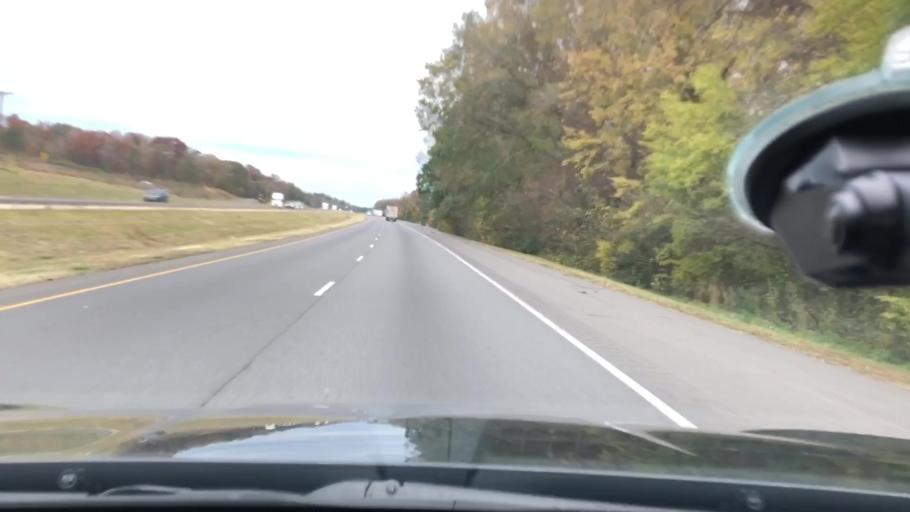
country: US
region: Arkansas
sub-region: Hot Spring County
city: Malvern
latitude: 34.3725
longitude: -92.8579
